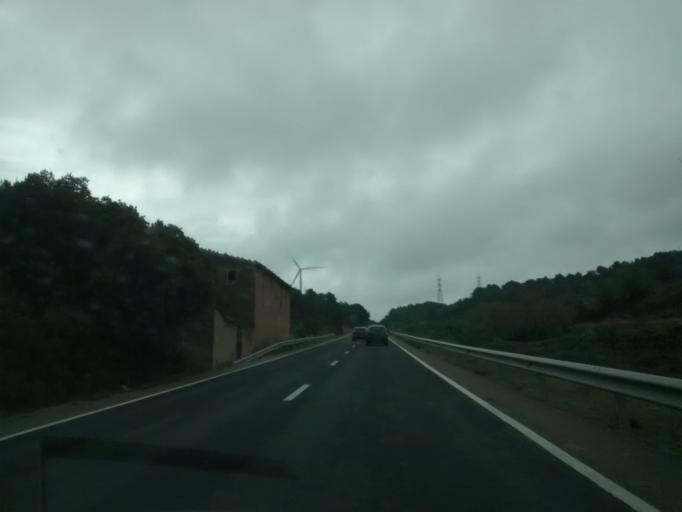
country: ES
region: Catalonia
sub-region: Provincia de Tarragona
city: Batea
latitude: 41.0613
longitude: 0.3510
